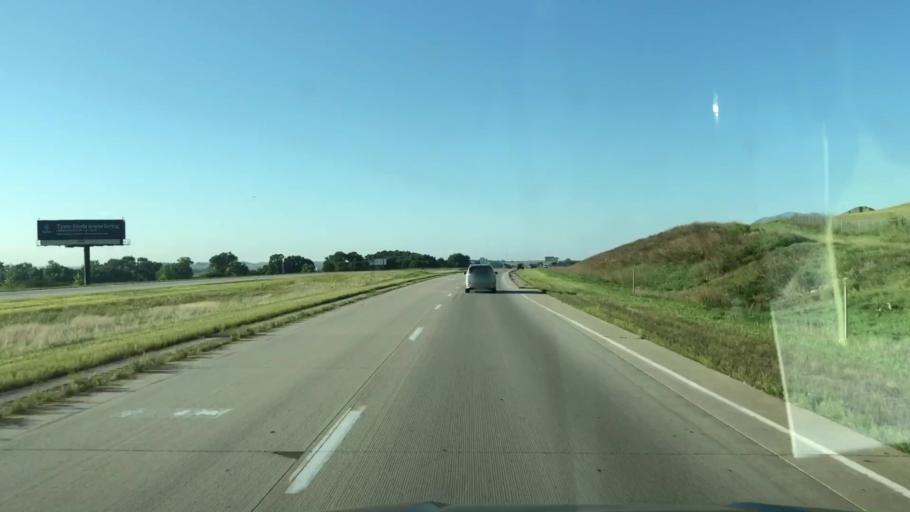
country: US
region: Iowa
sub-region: Plymouth County
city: Le Mars
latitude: 42.7572
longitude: -96.2095
